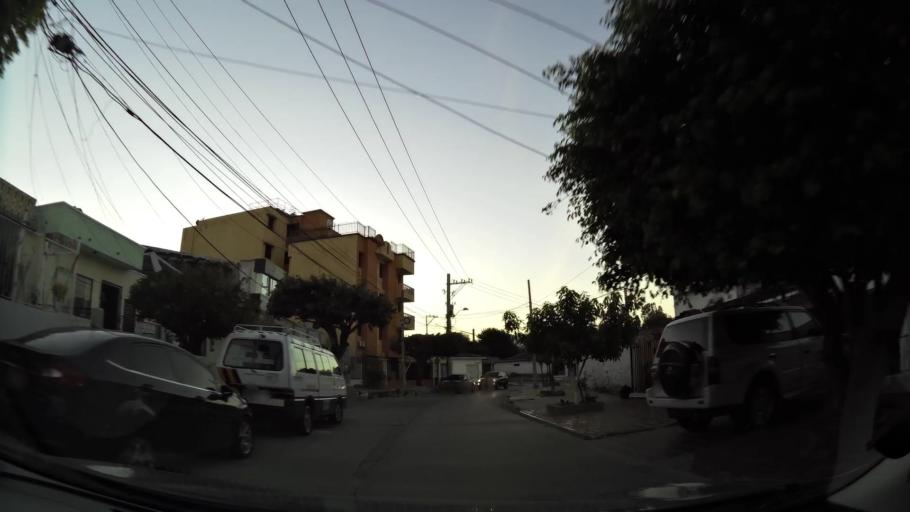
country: CO
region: Atlantico
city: Barranquilla
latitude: 10.9802
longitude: -74.8137
